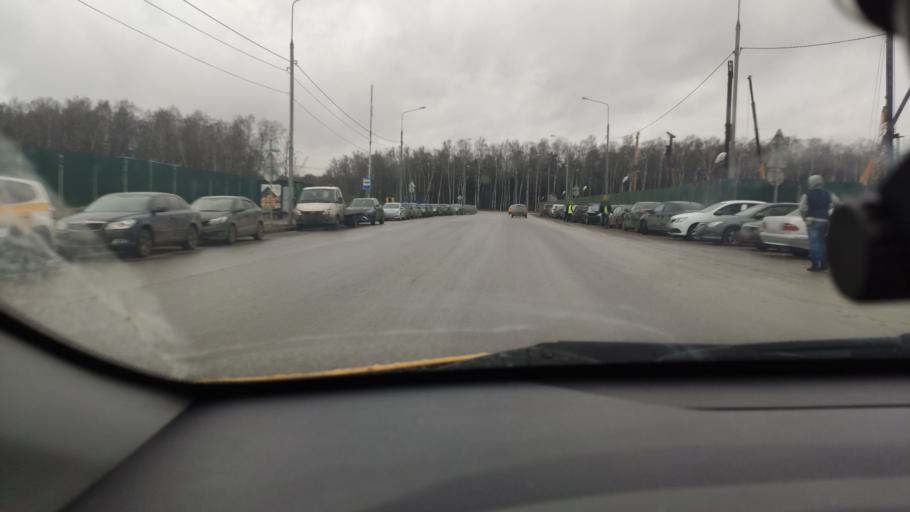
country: RU
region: Moscow
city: Annino
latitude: 55.5375
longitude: 37.6135
